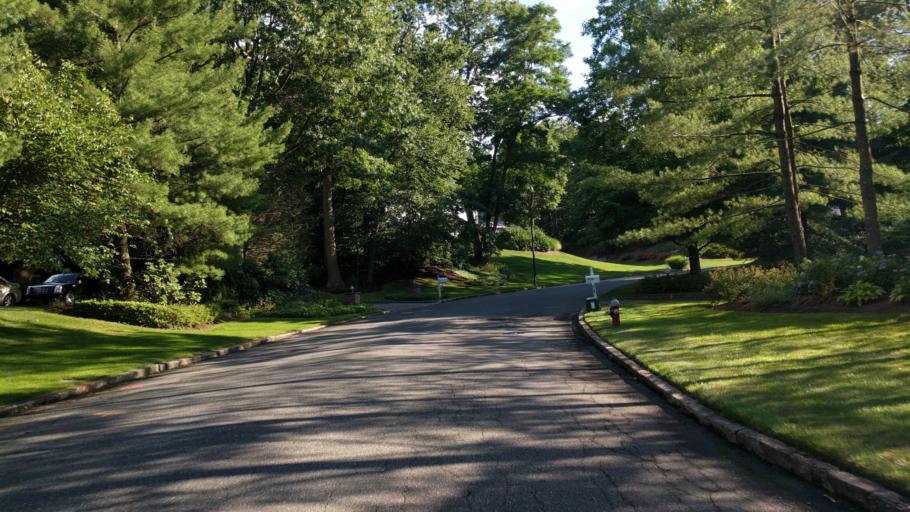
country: US
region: New York
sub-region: Nassau County
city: Oyster Bay
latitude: 40.8570
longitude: -73.5195
